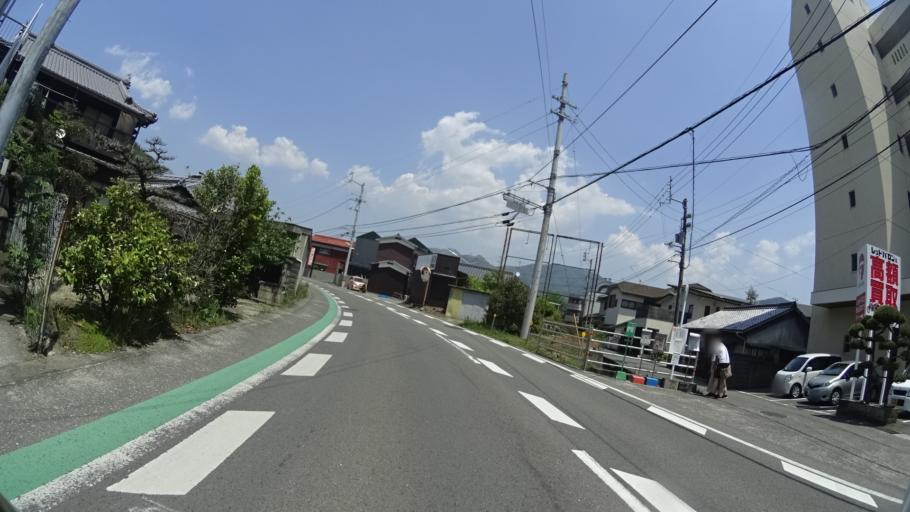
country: JP
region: Ehime
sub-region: Shikoku-chuo Shi
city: Matsuyama
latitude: 33.8469
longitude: 132.7982
